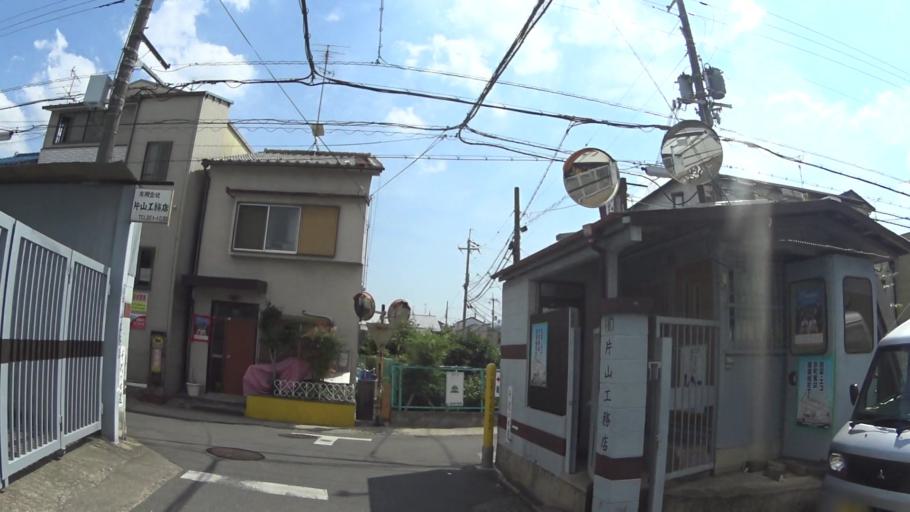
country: JP
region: Kyoto
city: Muko
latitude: 35.0057
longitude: 135.6939
